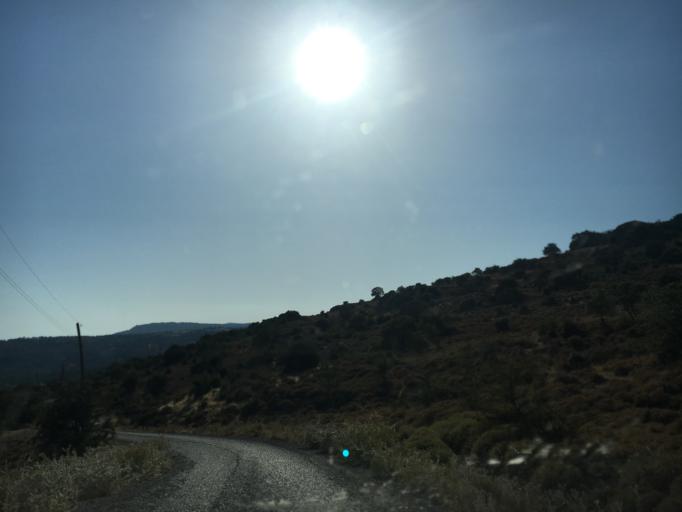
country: TR
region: Canakkale
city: Behram
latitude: 39.4855
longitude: 26.2683
